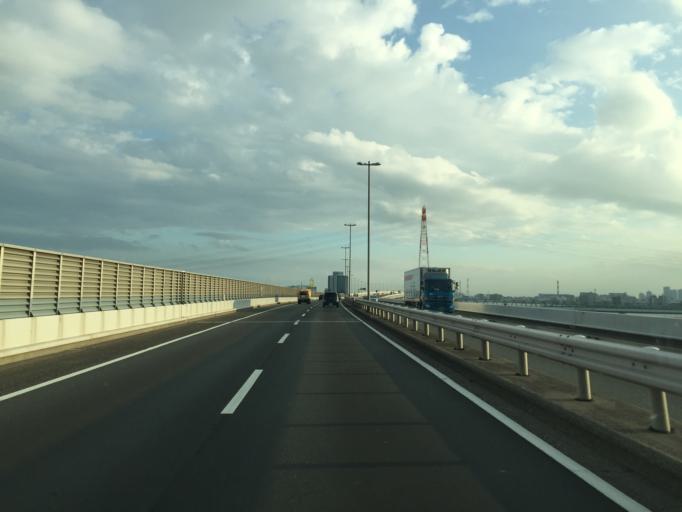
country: JP
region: Tokyo
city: Urayasu
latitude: 35.6924
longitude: 139.8596
